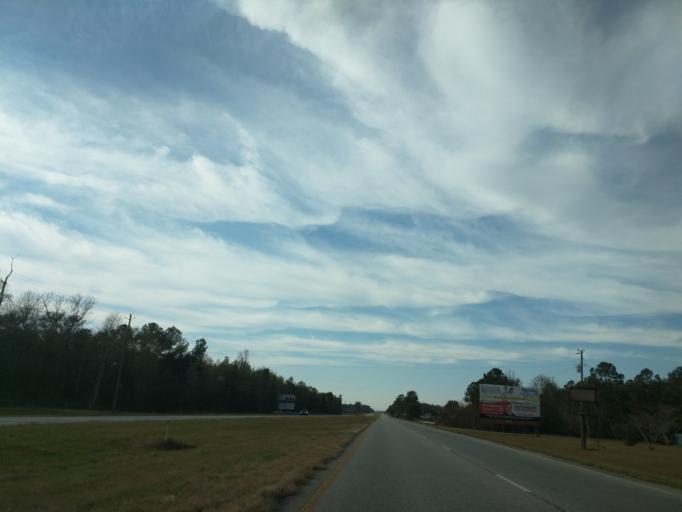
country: US
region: Georgia
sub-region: Decatur County
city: Bainbridge
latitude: 30.8907
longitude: -84.4887
